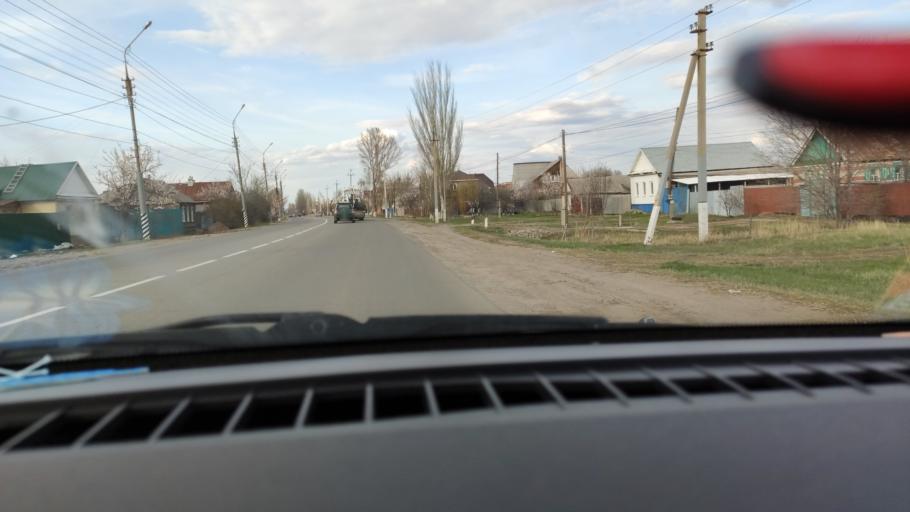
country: RU
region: Saratov
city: Privolzhskiy
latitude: 51.4316
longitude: 46.0557
